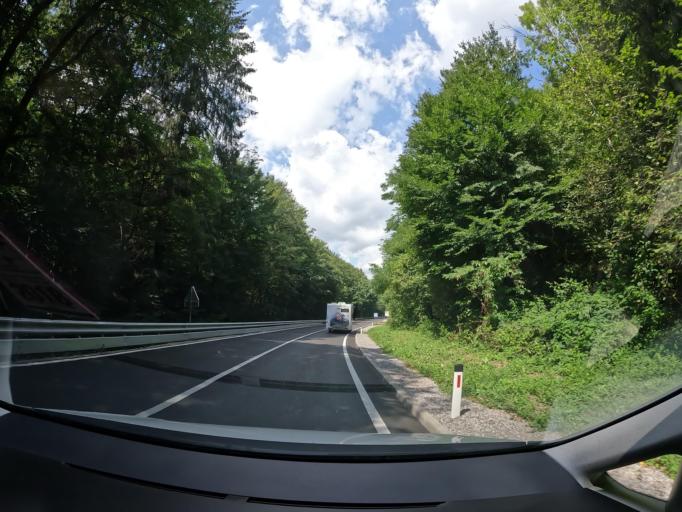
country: SI
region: Ilirska Bistrica
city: Ilirska Bistrica
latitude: 45.5229
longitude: 14.2491
